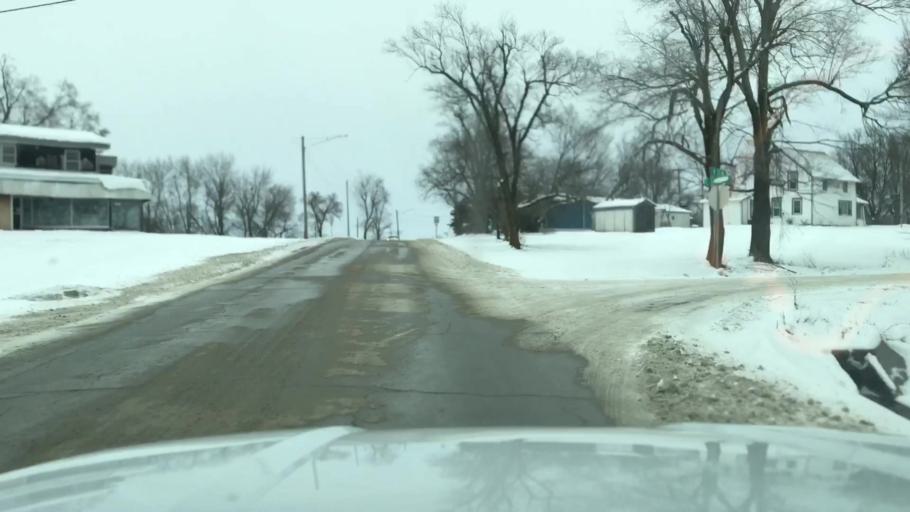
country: US
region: Missouri
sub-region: Clinton County
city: Cameron
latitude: 39.7461
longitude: -94.2304
